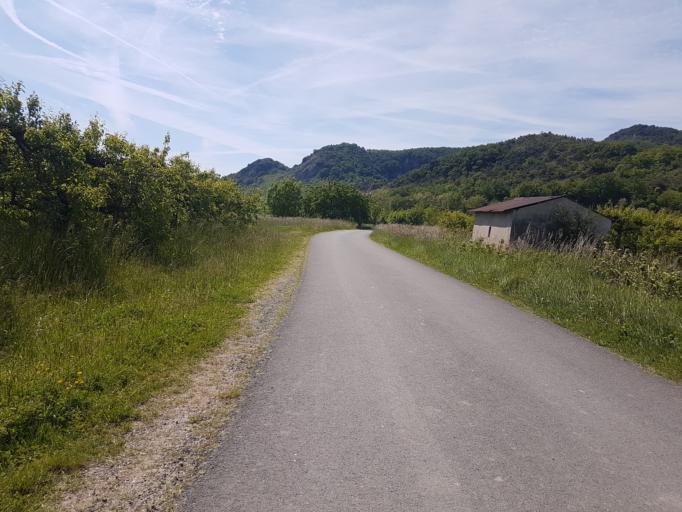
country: FR
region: Rhone-Alpes
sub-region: Departement de l'Ardeche
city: Le Pouzin
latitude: 44.7204
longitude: 4.7563
